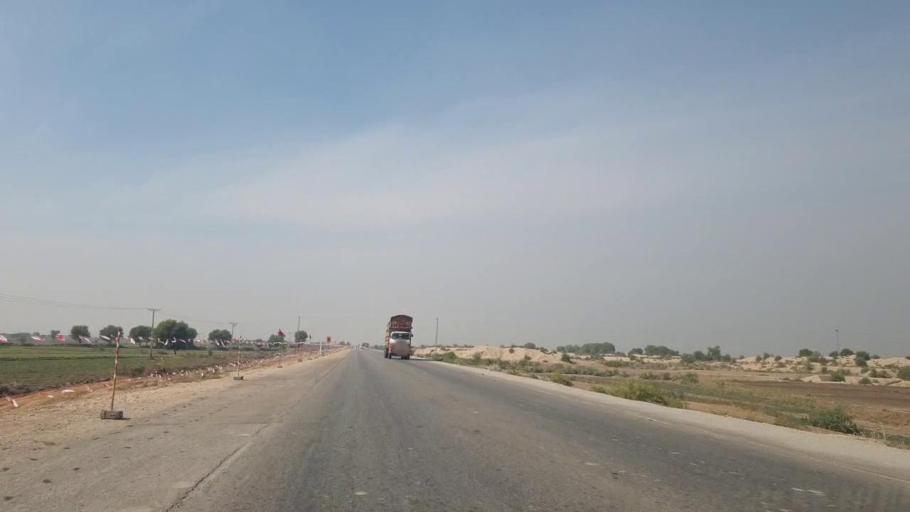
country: PK
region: Sindh
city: Sann
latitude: 25.9906
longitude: 68.1756
